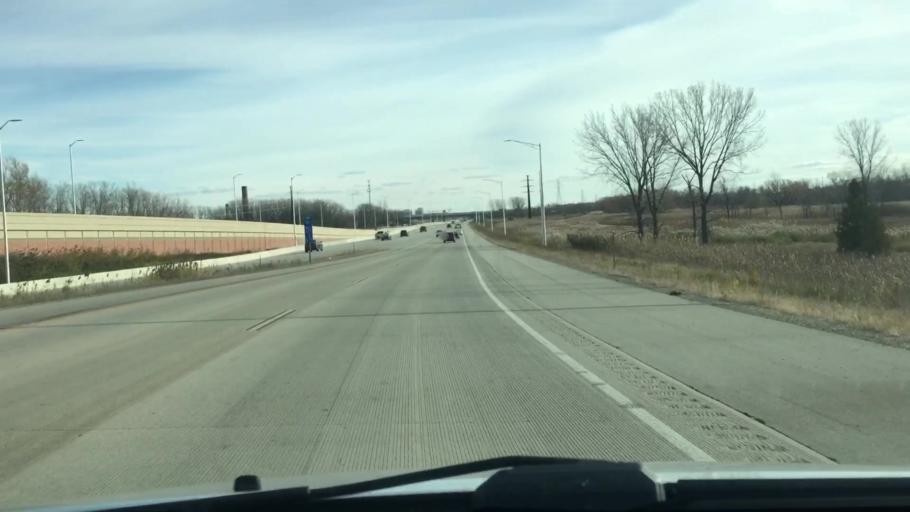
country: US
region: Wisconsin
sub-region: Brown County
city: Howard
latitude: 44.5578
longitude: -88.0501
